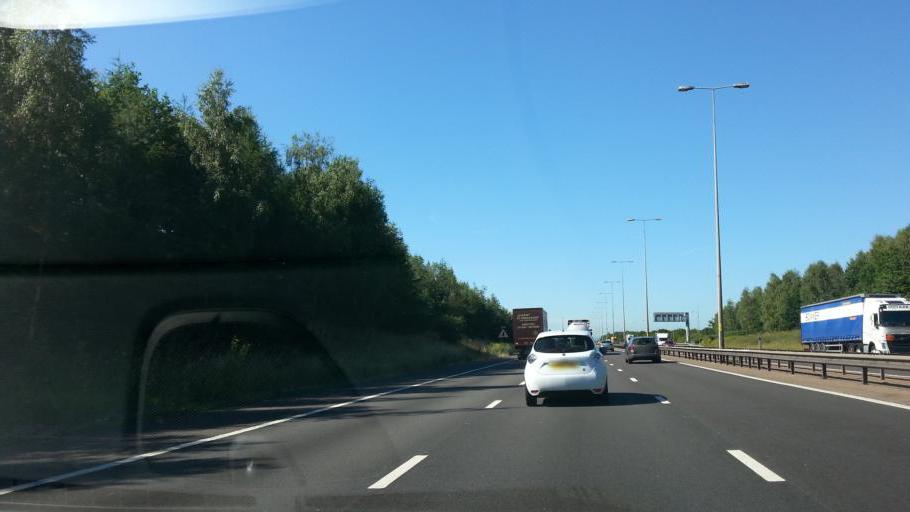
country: GB
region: England
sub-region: Worcestershire
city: Worcester
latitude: 52.1677
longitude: -2.1807
